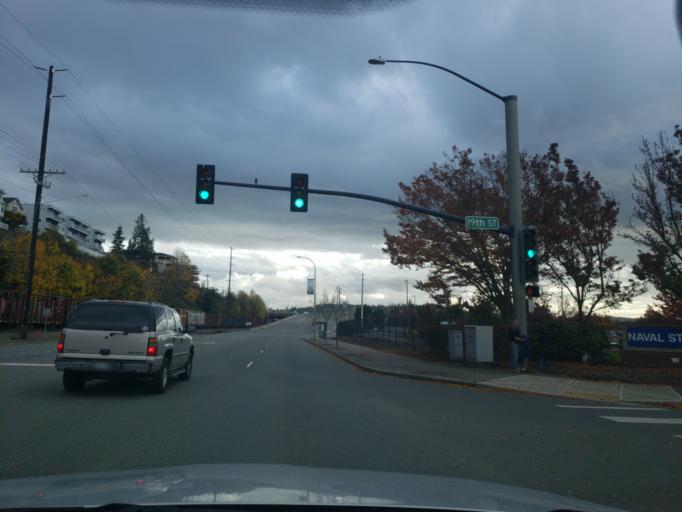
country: US
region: Washington
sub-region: Snohomish County
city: Everett
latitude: 47.9925
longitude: -122.2139
